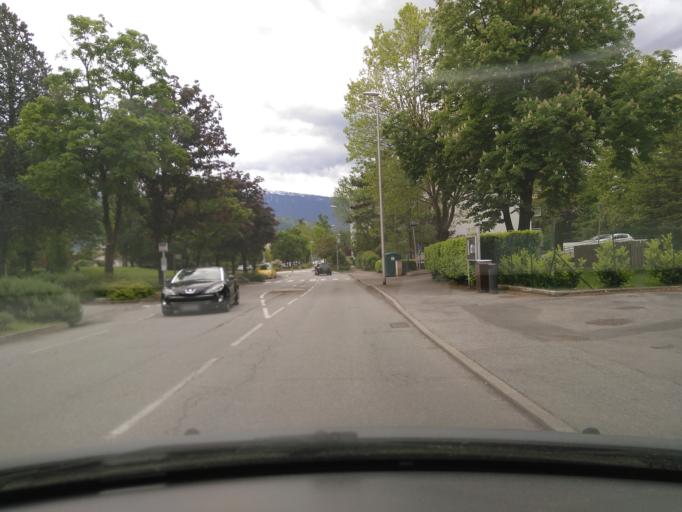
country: FR
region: Rhone-Alpes
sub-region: Departement de l'Isere
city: Corenc
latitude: 45.2054
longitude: 5.7583
